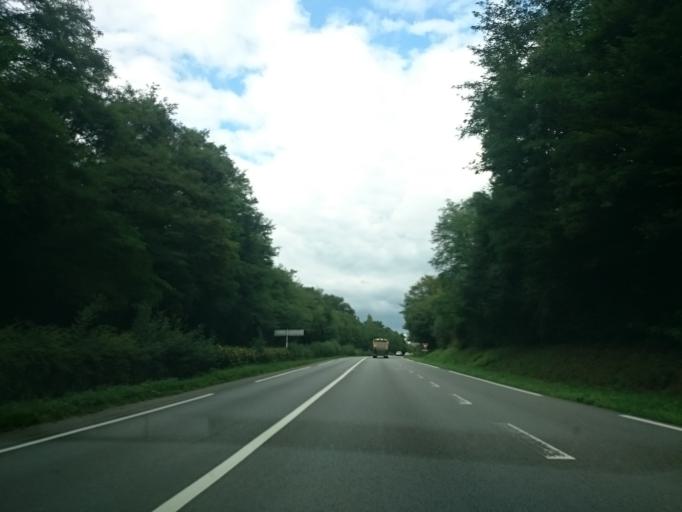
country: FR
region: Pays de la Loire
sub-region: Departement de la Loire-Atlantique
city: Orvault
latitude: 47.2456
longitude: -1.6352
